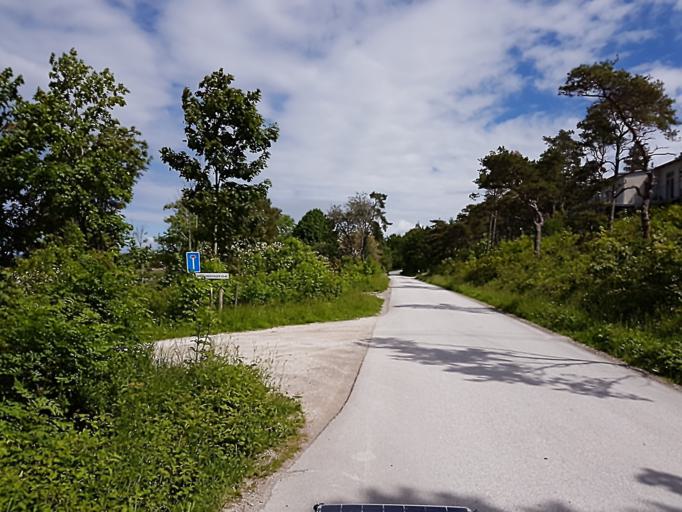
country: SE
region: Gotland
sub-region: Gotland
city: Visby
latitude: 57.7158
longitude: 18.3838
